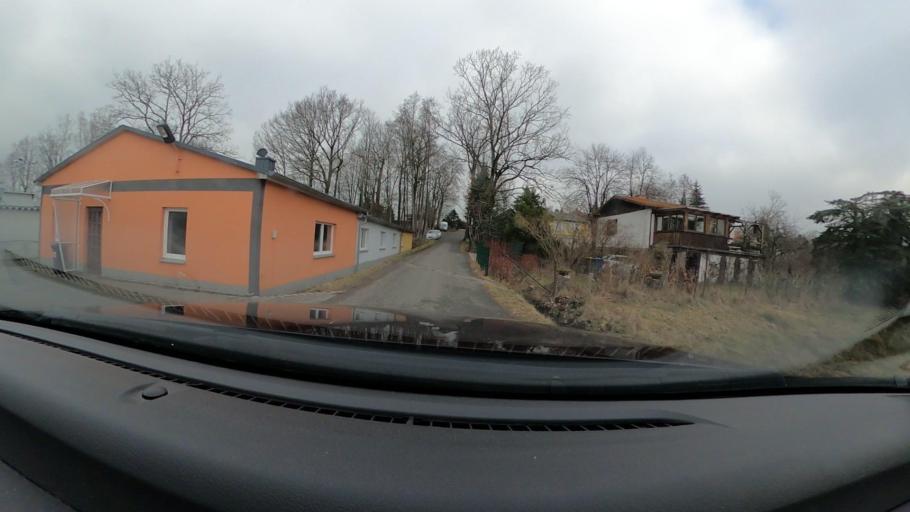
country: DE
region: Saxony
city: Oberschona
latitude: 50.9072
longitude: 13.2906
